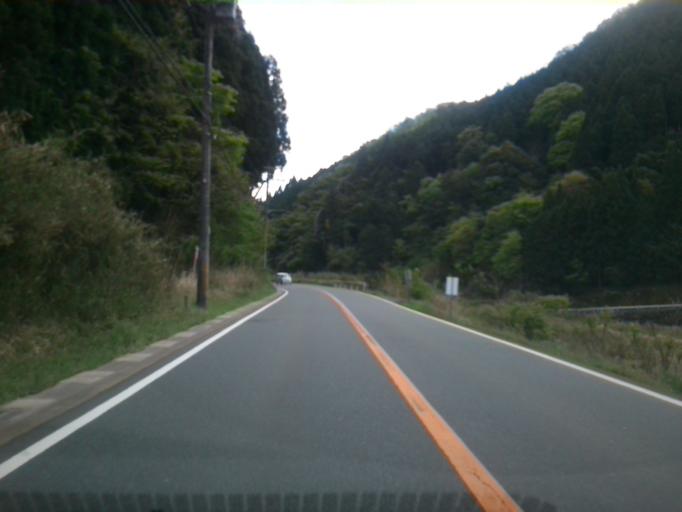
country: JP
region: Kyoto
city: Fukuchiyama
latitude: 35.3395
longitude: 135.0687
